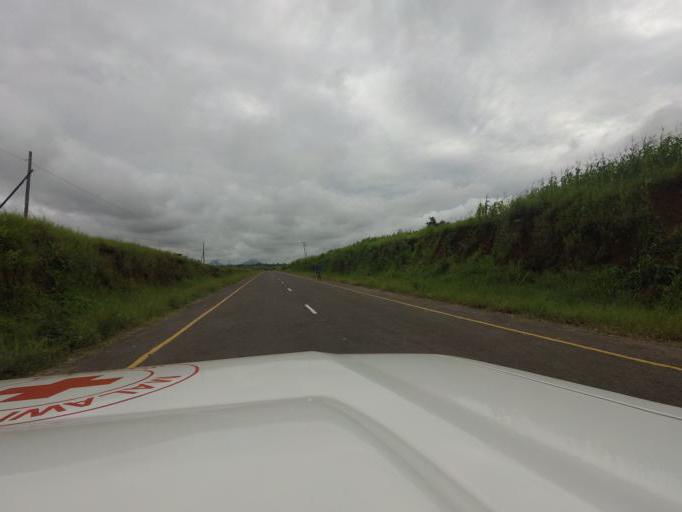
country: MW
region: Southern Region
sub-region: Thyolo District
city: Thyolo
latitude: -16.0053
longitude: 35.1771
